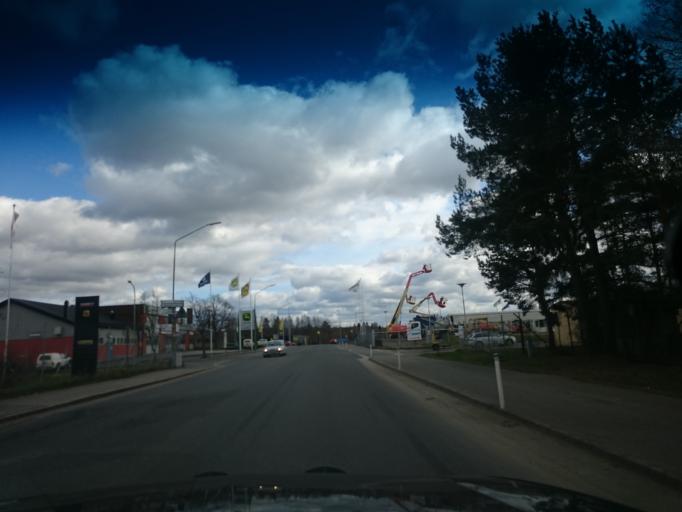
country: SE
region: Joenkoeping
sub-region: Vetlanda Kommun
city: Vetlanda
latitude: 57.4152
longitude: 15.0853
